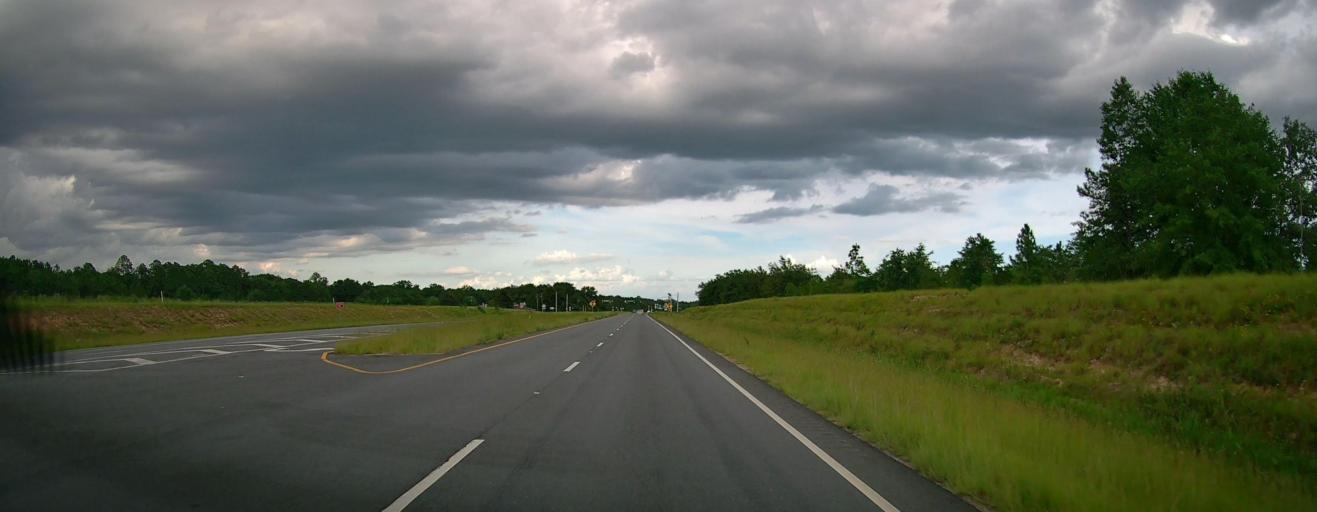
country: US
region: Georgia
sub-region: Taylor County
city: Butler
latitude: 32.5457
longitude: -84.2470
